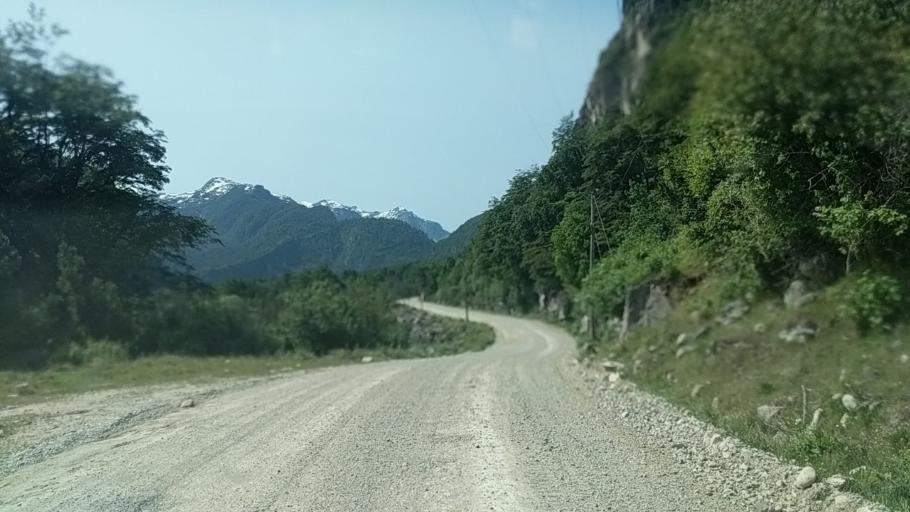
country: CL
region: Los Lagos
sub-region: Provincia de Palena
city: Palena
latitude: -43.4661
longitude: -72.1104
